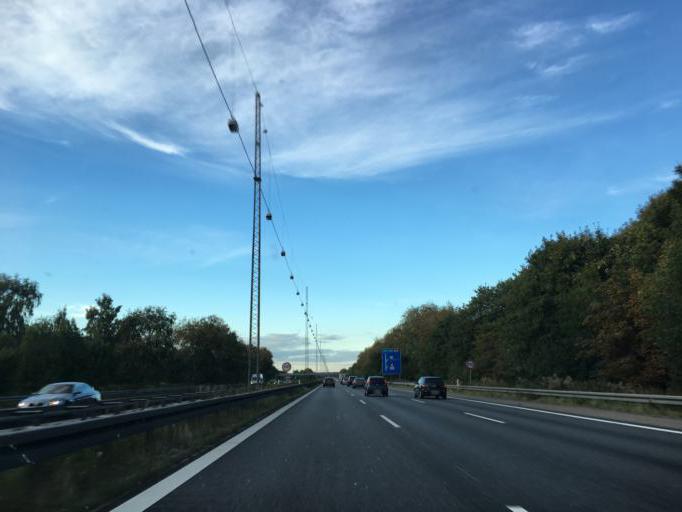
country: DK
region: Capital Region
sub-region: Lyngby-Tarbaek Kommune
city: Kongens Lyngby
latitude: 55.7830
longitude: 12.5273
